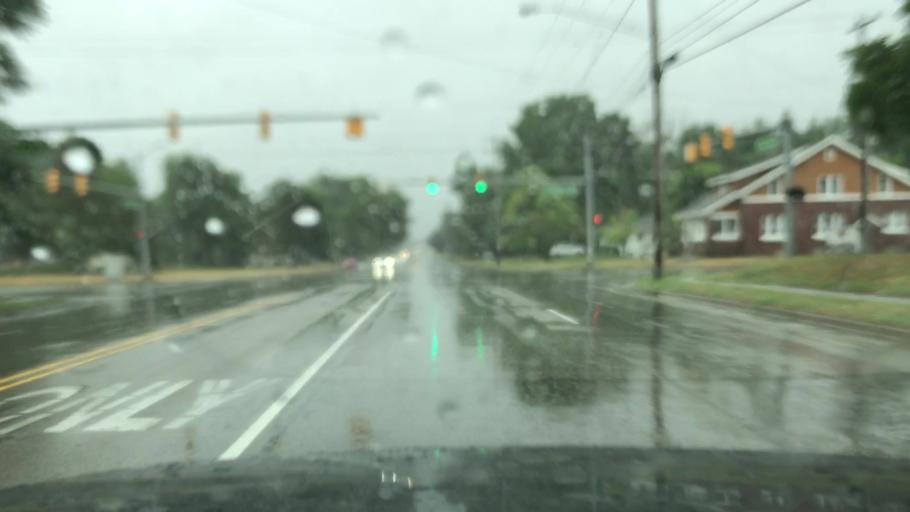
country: US
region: Michigan
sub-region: Kent County
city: Wyoming
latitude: 42.9070
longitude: -85.7247
